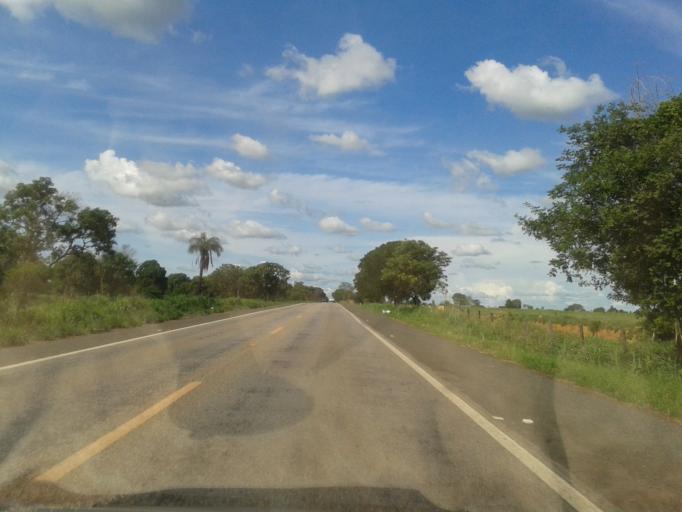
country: BR
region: Goias
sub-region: Mozarlandia
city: Mozarlandia
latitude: -15.0595
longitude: -50.6132
